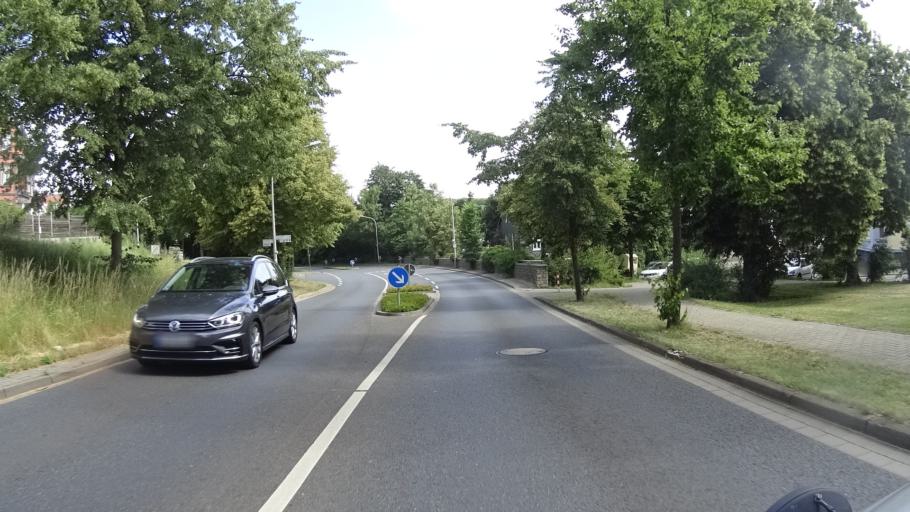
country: DE
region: Lower Saxony
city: Goslar
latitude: 51.9089
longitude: 10.4171
